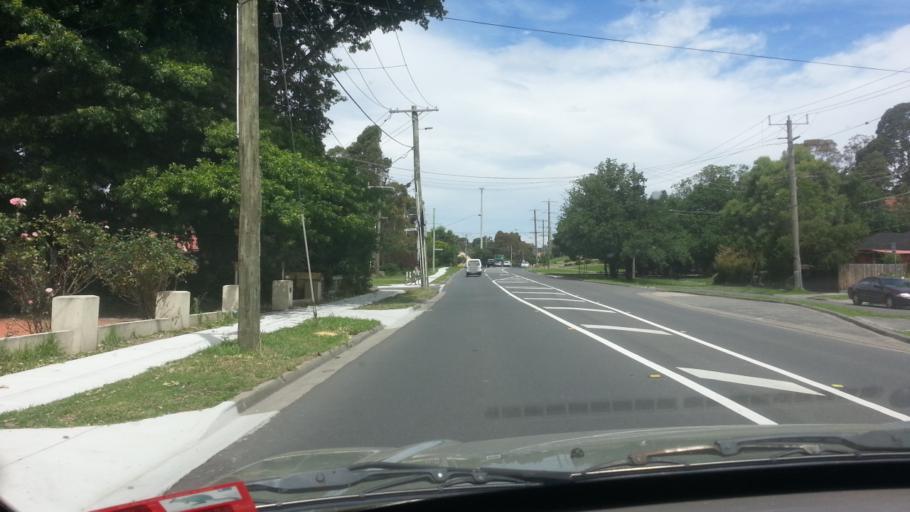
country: AU
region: Victoria
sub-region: Knox
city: Ferntree Gully
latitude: -37.8912
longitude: 145.2900
